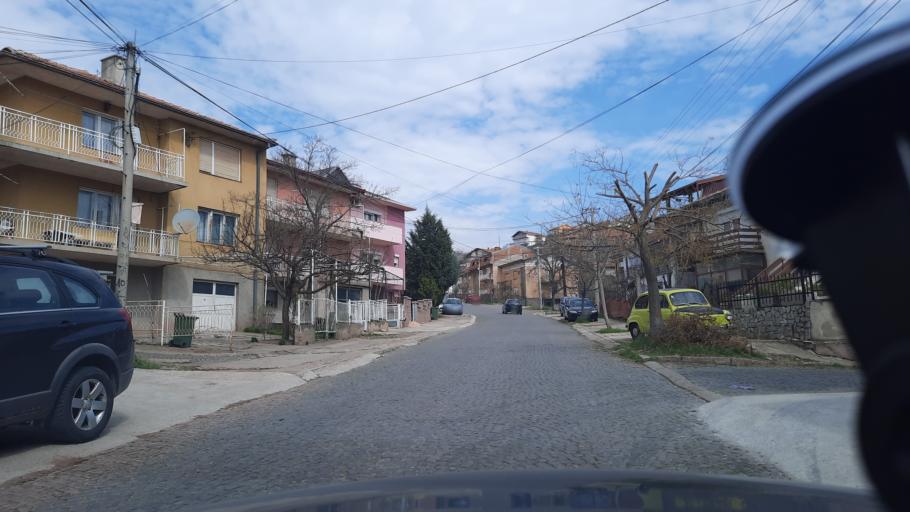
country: MK
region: Stip
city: Shtip
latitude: 41.7453
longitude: 22.1998
